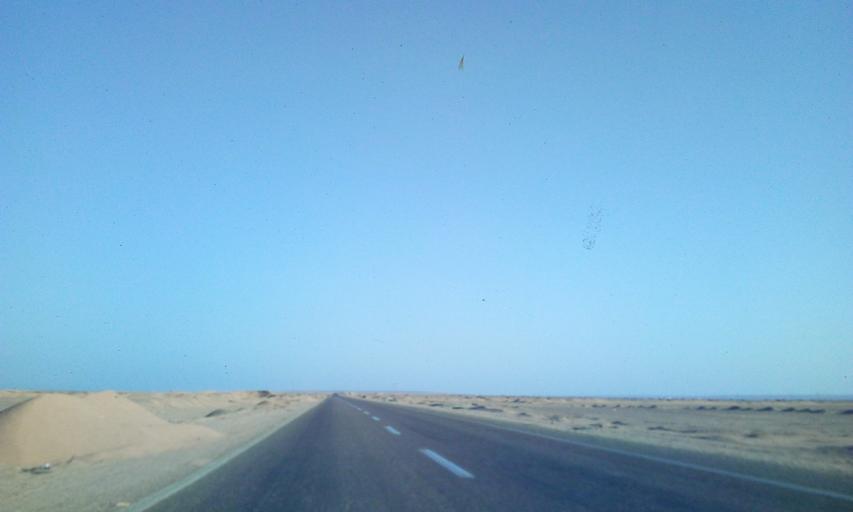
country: EG
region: South Sinai
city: Tor
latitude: 28.4442
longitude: 33.0000
